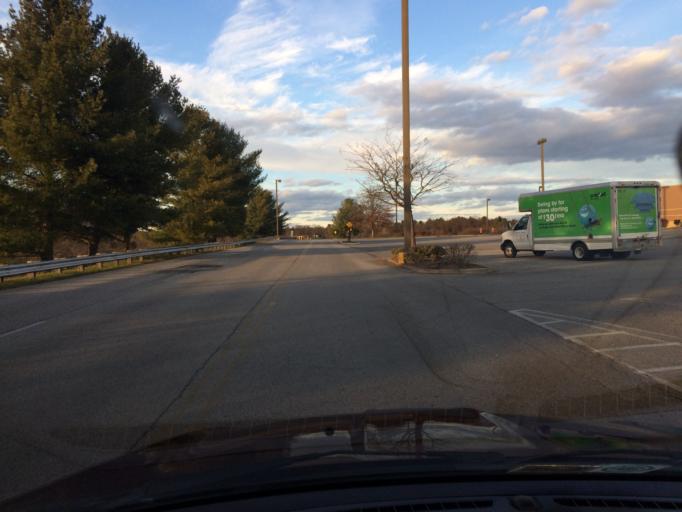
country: US
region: Virginia
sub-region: Montgomery County
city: Merrimac
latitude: 37.1657
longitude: -80.4295
